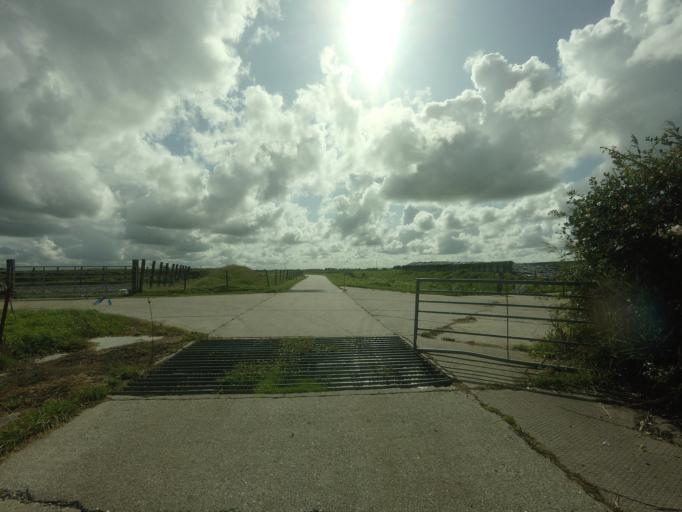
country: NL
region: Friesland
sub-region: Sudwest Fryslan
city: Scharnegoutum
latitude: 53.0714
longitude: 5.6373
